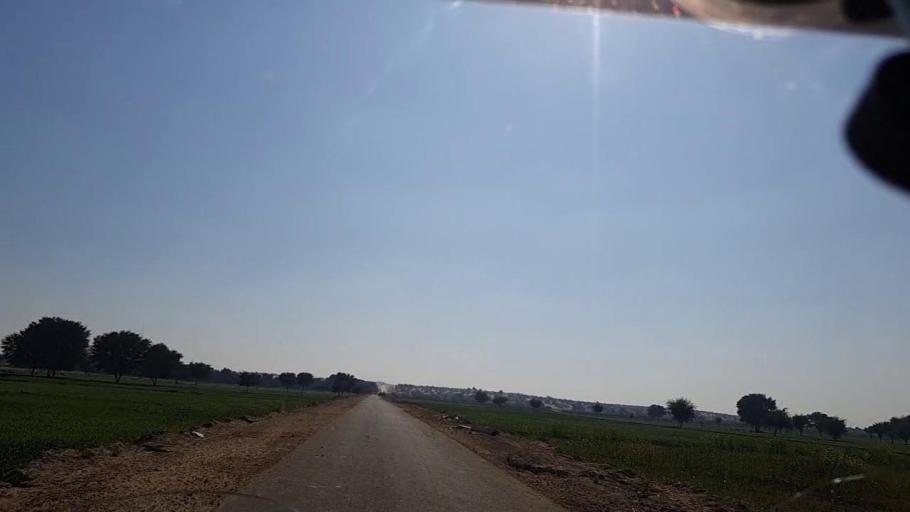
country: PK
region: Sindh
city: Khanpur
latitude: 27.5705
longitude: 69.3888
